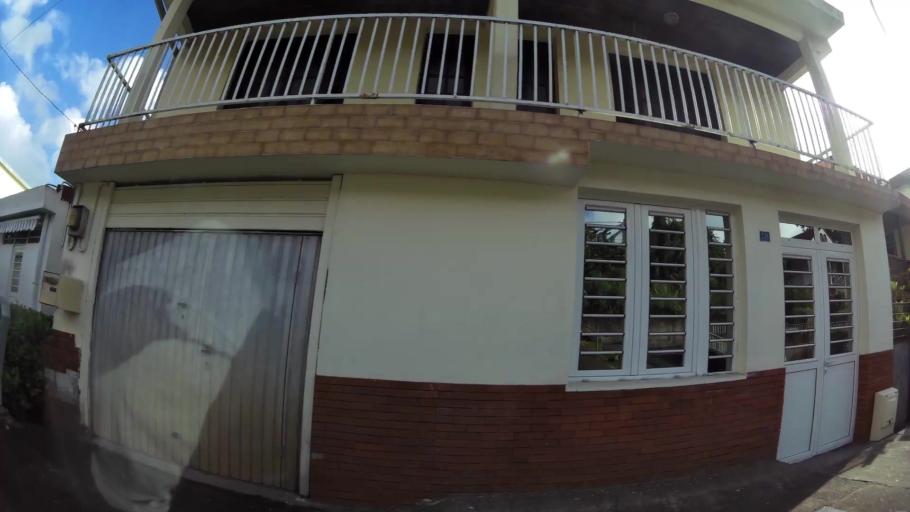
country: MQ
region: Martinique
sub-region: Martinique
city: Ducos
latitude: 14.5463
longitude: -60.9649
